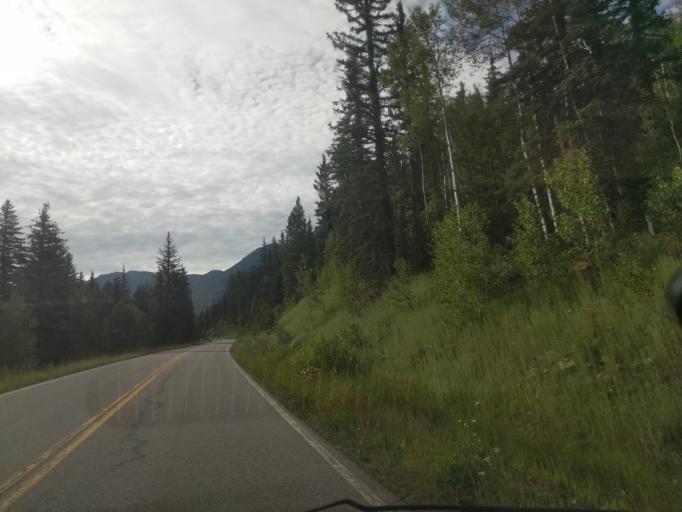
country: US
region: Colorado
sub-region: Garfield County
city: Carbondale
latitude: 39.0894
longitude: -107.2501
